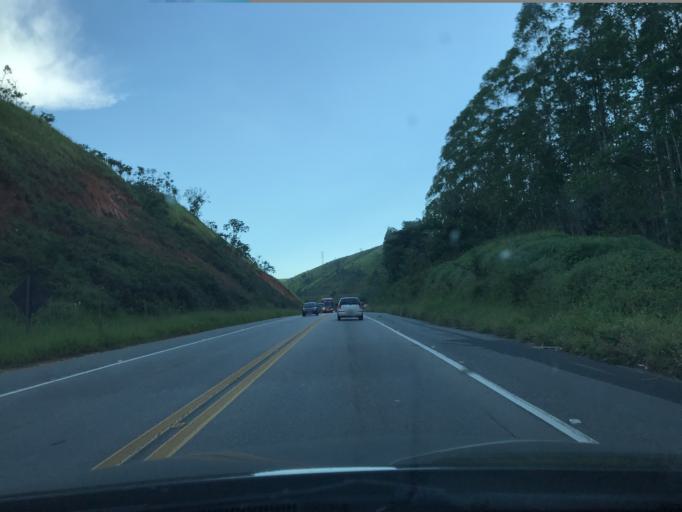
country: BR
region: Sao Paulo
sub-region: Tremembe
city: Tremembe
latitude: -22.8727
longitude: -45.5963
